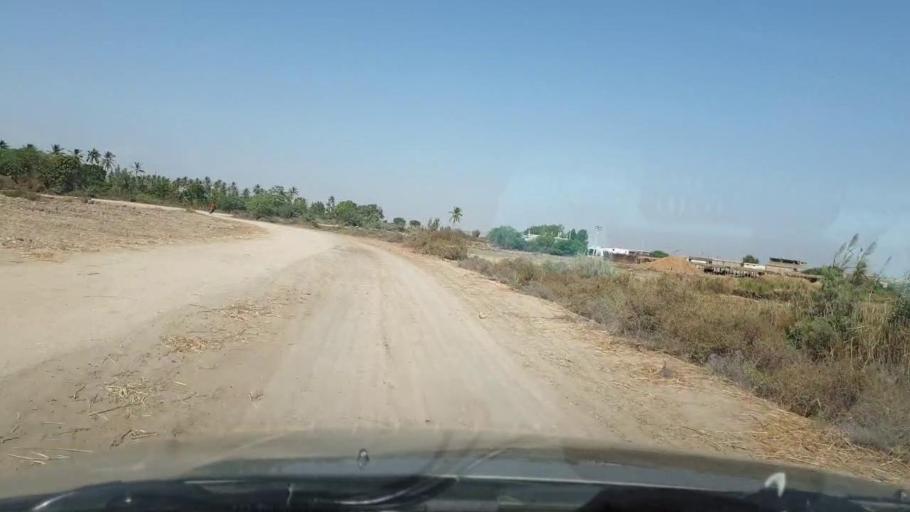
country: PK
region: Sindh
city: Thatta
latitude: 24.6340
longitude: 67.8948
